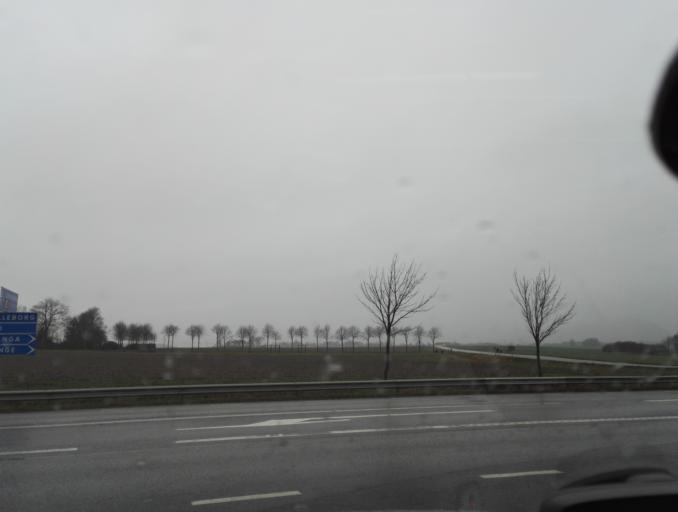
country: SE
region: Skane
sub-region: Kavlinge Kommun
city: Kaevlinge
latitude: 55.7680
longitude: 13.1334
